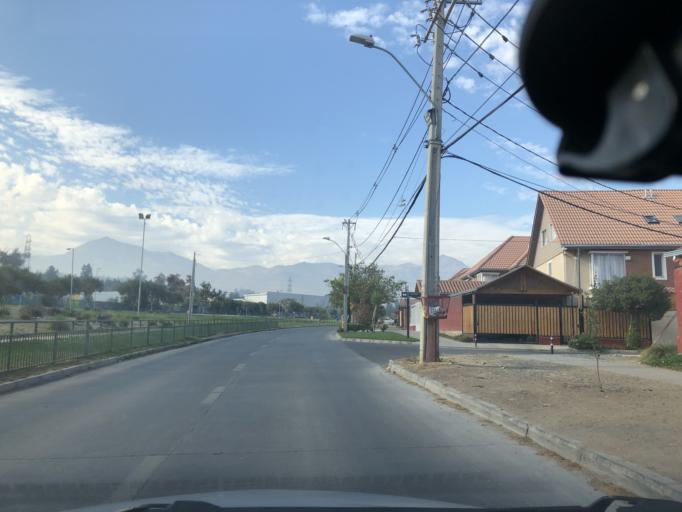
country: CL
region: Santiago Metropolitan
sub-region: Provincia de Cordillera
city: Puente Alto
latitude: -33.5896
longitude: -70.5442
